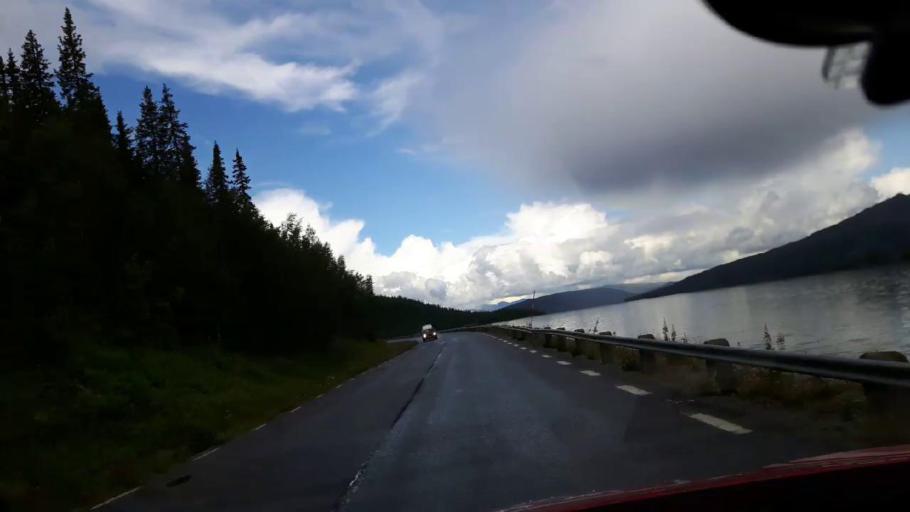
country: SE
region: Vaesterbotten
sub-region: Vilhelmina Kommun
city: Sjoberg
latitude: 64.9800
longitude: 15.3100
